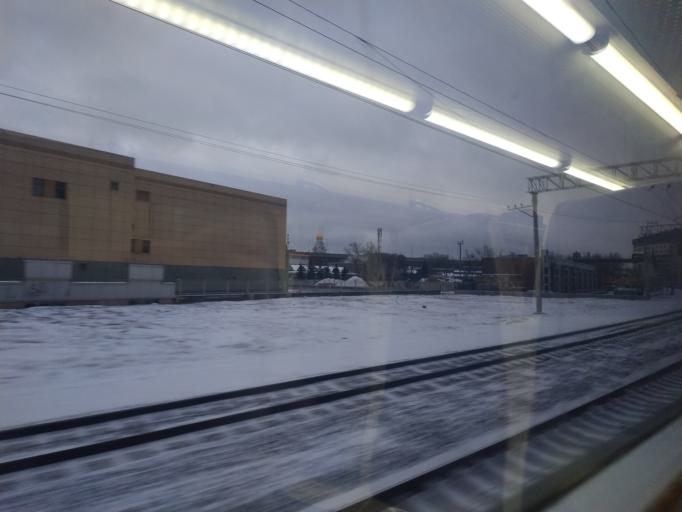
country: RU
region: Moscow
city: Taganskiy
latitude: 55.7412
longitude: 37.6919
